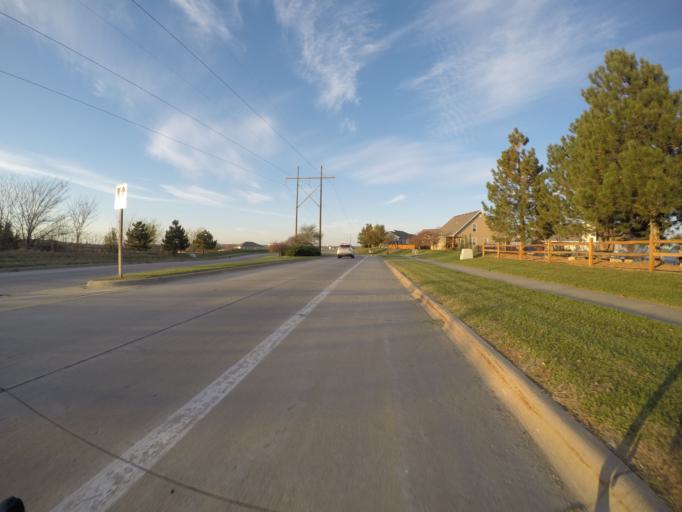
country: US
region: Kansas
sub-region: Riley County
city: Manhattan
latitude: 39.1732
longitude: -96.6207
